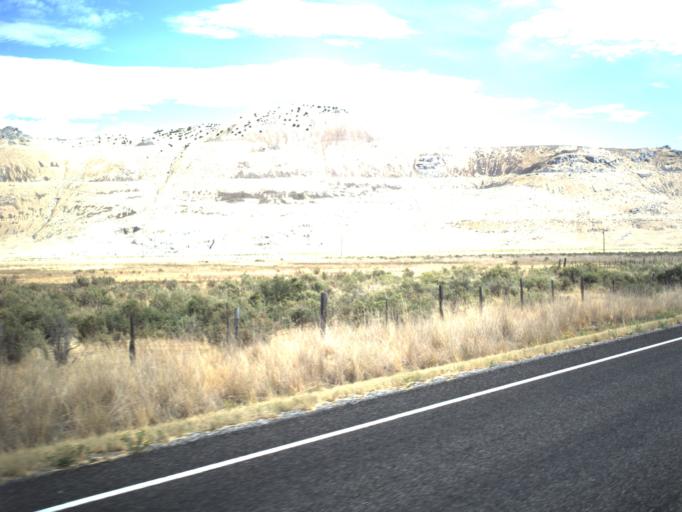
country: US
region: Utah
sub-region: Box Elder County
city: Tremonton
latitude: 41.5928
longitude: -112.2798
